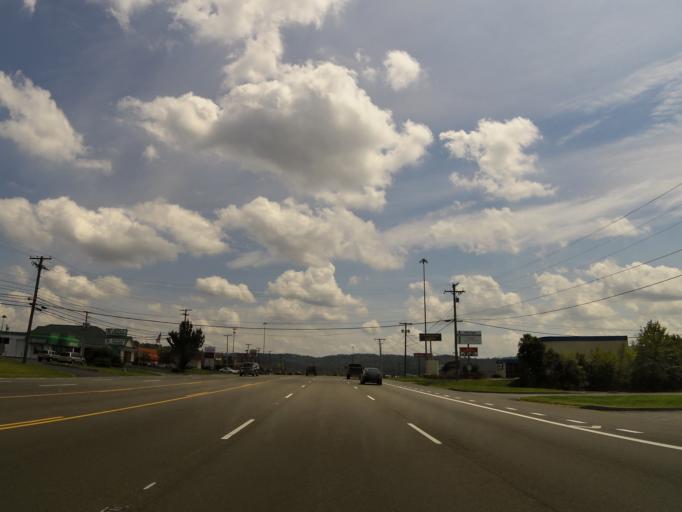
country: US
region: Tennessee
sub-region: Sullivan County
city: Kingsport
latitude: 36.5496
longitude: -82.5234
